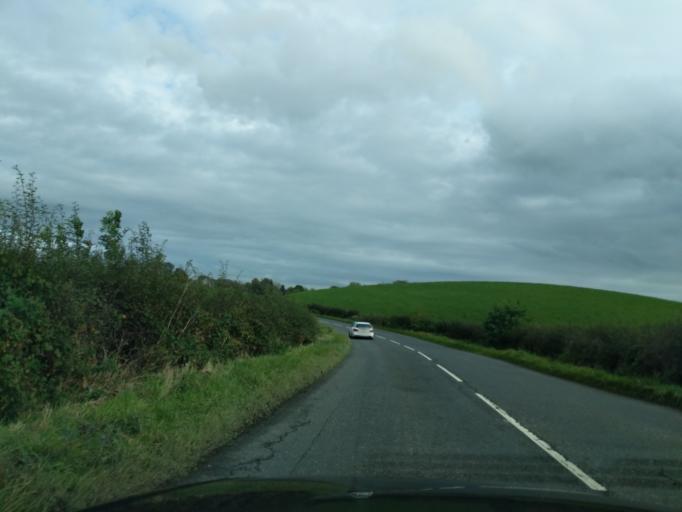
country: GB
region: Scotland
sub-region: Dumfries and Galloway
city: Castle Douglas
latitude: 54.9293
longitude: -3.9449
